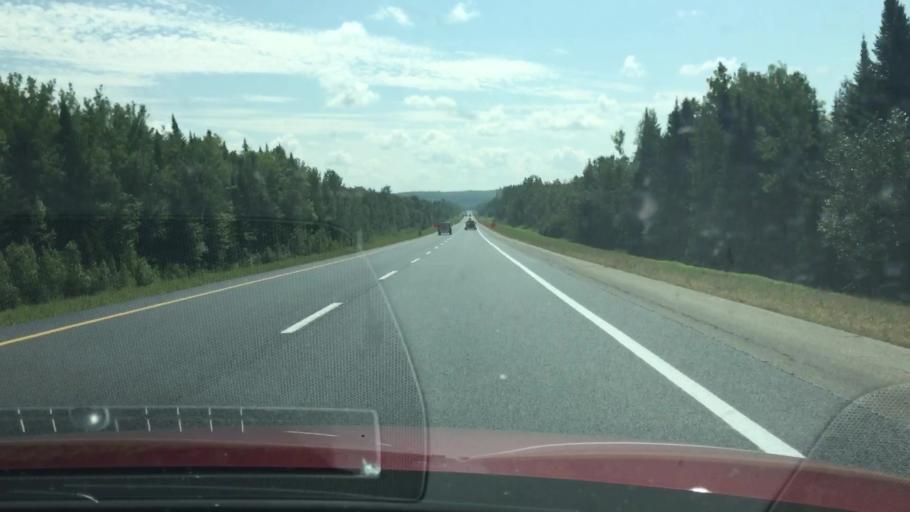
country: US
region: Maine
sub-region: Penobscot County
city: Patten
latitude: 45.8270
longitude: -68.4324
